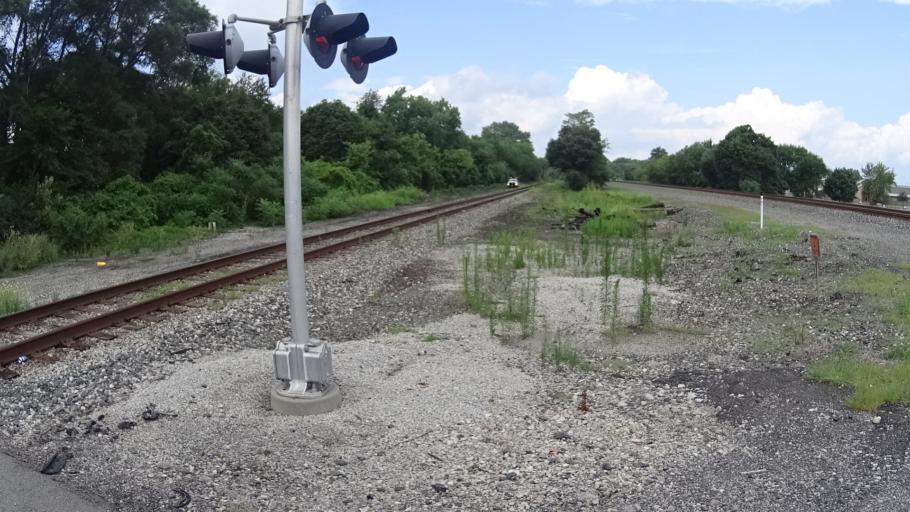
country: US
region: Ohio
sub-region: Erie County
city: Sandusky
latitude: 41.4411
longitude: -82.7275
